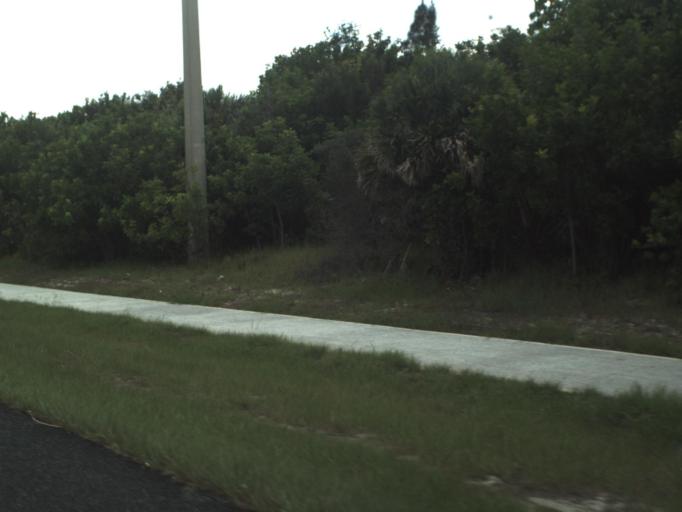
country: US
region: Florida
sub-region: Palm Beach County
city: Tequesta
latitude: 26.9802
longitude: -80.0907
